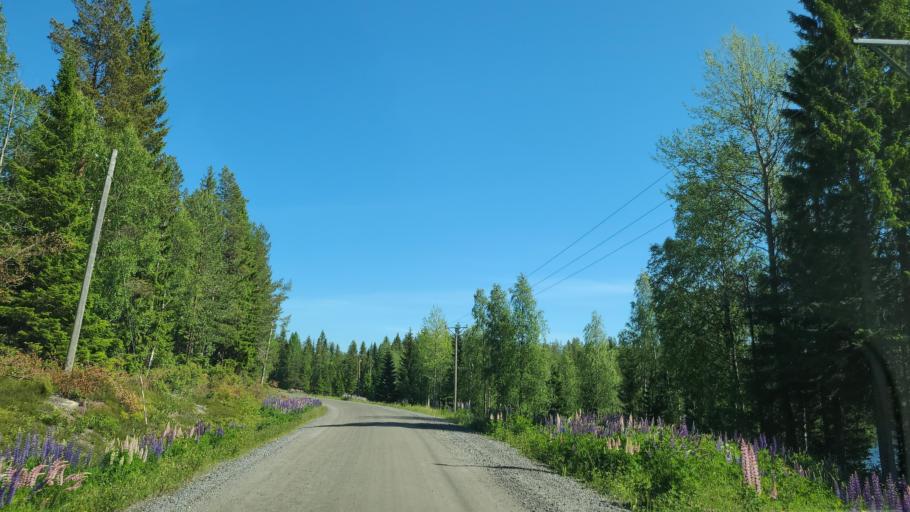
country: SE
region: Vaesterbotten
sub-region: Bjurholms Kommun
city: Bjurholm
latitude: 63.6397
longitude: 19.1448
